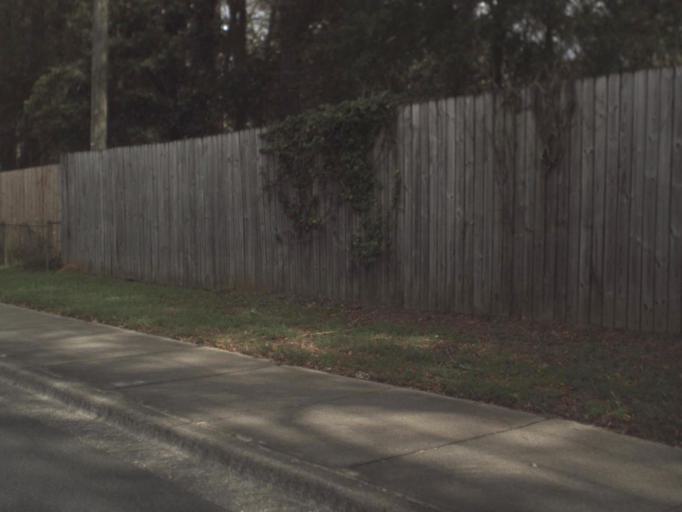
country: US
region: Florida
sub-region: Leon County
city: Tallahassee
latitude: 30.5325
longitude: -84.2331
